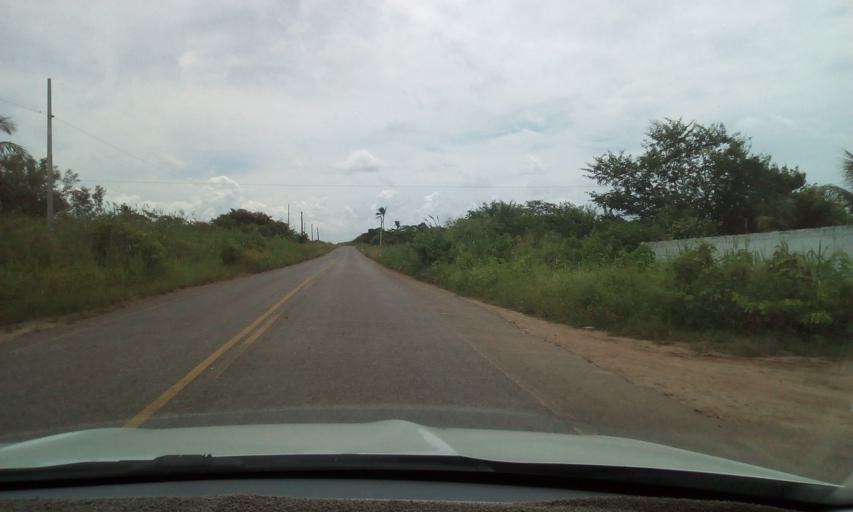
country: BR
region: Paraiba
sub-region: Mari
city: Mari
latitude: -7.1177
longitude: -35.3406
